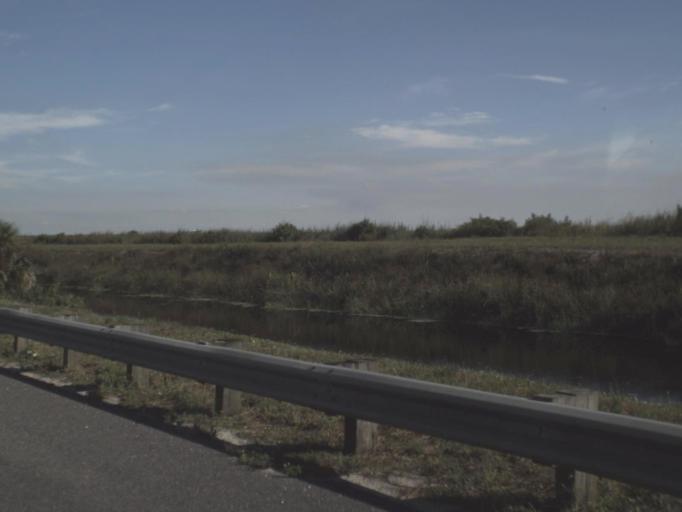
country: US
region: Florida
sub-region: Glades County
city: Moore Haven
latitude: 26.7535
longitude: -81.0622
